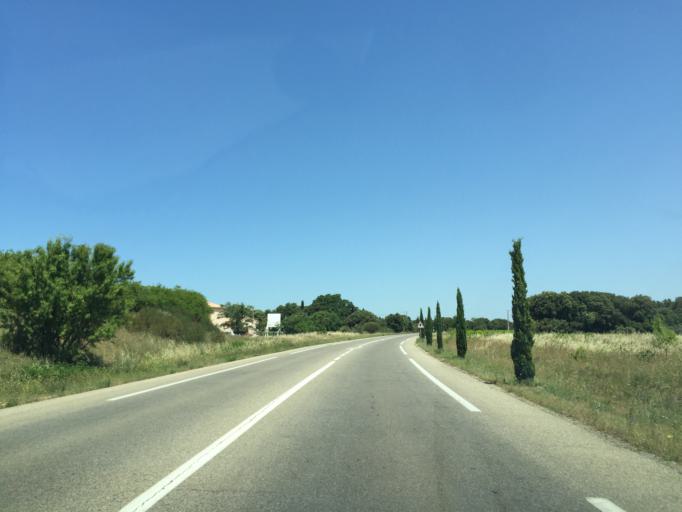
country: FR
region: Provence-Alpes-Cote d'Azur
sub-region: Departement du Vaucluse
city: Serignan-du-Comtat
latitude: 44.1838
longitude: 4.8548
